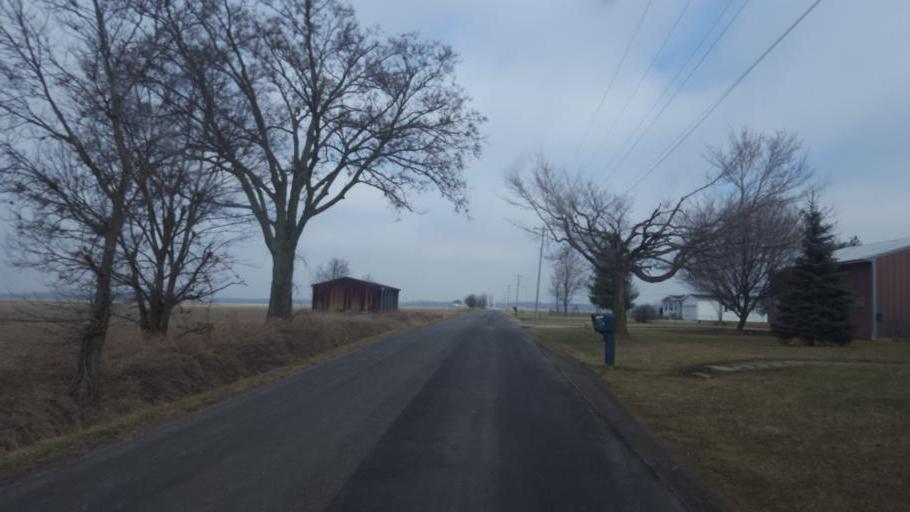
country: US
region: Ohio
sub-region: Morrow County
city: Mount Gilead
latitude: 40.6338
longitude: -82.8600
